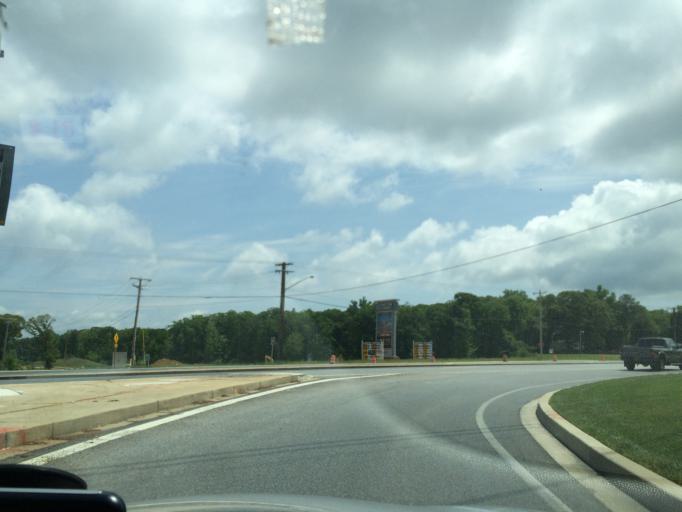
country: US
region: Maryland
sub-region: Saint Mary's County
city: California
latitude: 38.3084
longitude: -76.5307
